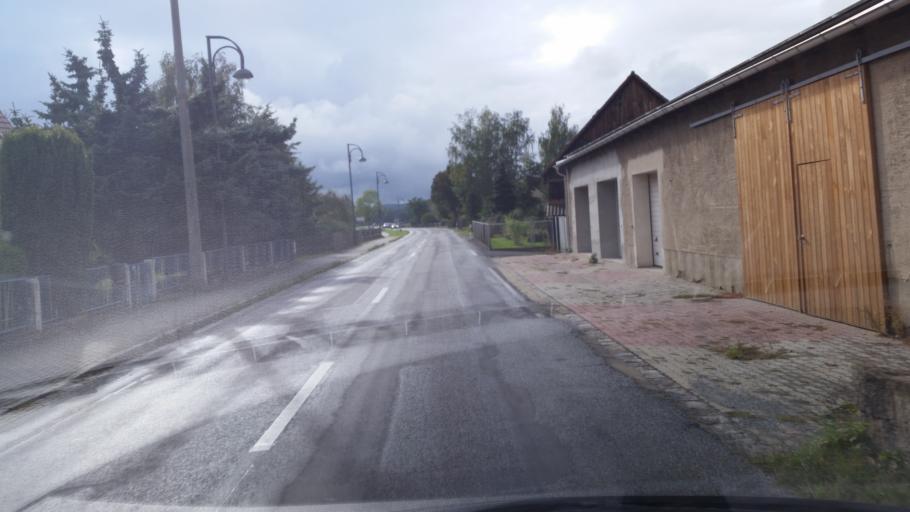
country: DE
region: Saxony
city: Kamenz
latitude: 51.3018
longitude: 14.1241
